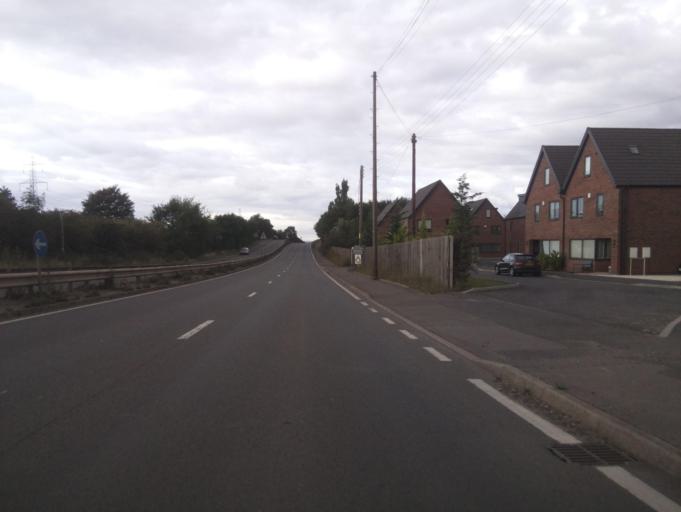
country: GB
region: England
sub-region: Warwickshire
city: Water Orton
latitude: 52.5101
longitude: -1.7160
